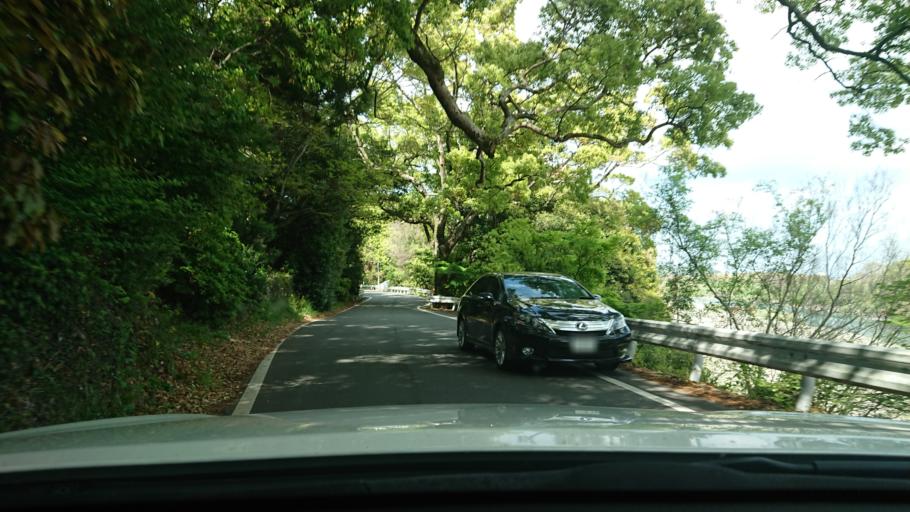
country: JP
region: Tokushima
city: Komatsushimacho
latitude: 34.0044
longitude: 134.5510
